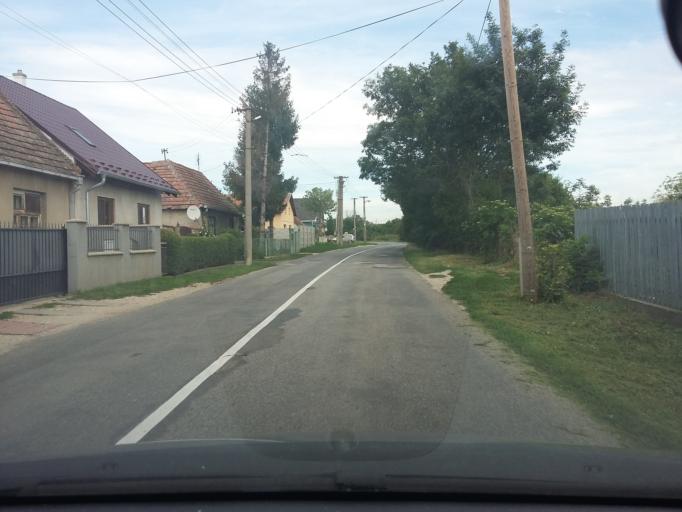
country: SK
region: Bratislavsky
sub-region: Okres Pezinok
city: Pezinok
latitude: 48.2562
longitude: 17.2837
